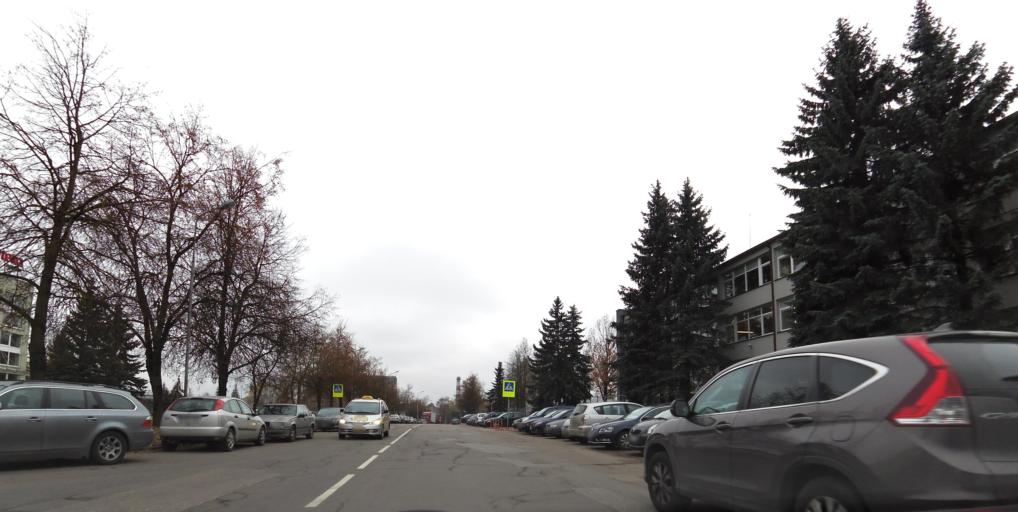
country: LT
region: Vilnius County
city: Vilkpede
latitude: 54.6397
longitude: 25.2668
